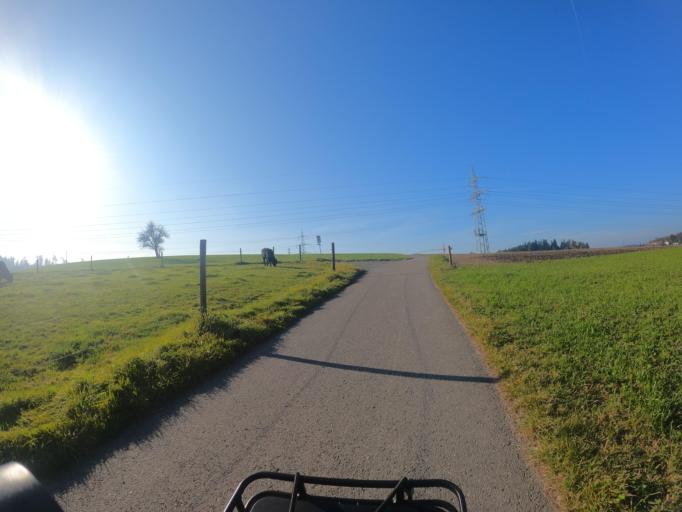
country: CH
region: Zurich
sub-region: Bezirk Affoltern
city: Obfelden / Toussen
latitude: 47.2875
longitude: 8.4266
